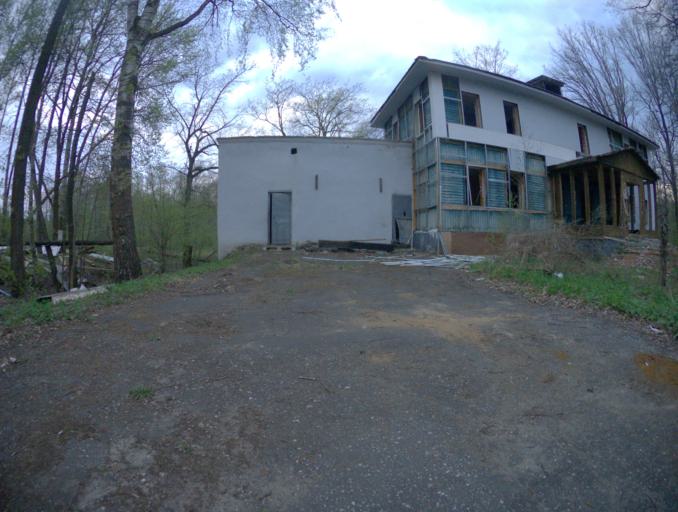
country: RU
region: Vladimir
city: Raduzhnyy
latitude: 56.0433
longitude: 40.3773
